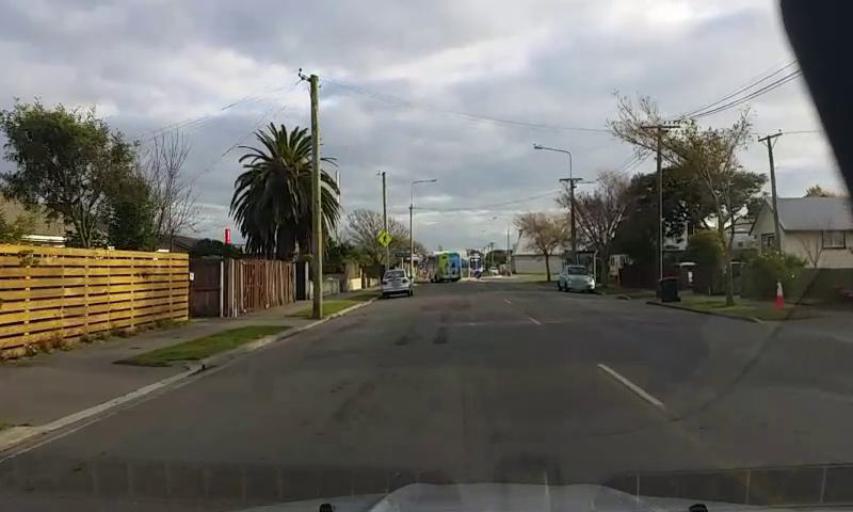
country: NZ
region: Canterbury
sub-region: Christchurch City
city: Christchurch
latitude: -43.5242
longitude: 172.7331
